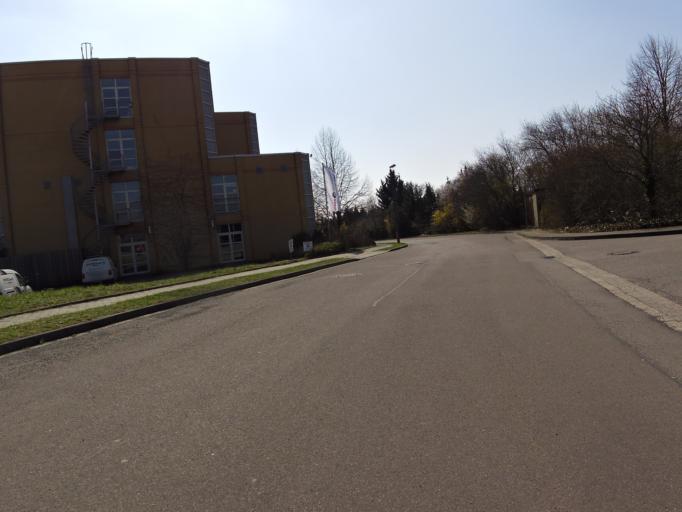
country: DE
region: Saxony
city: Leipzig
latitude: 51.3788
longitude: 12.3122
